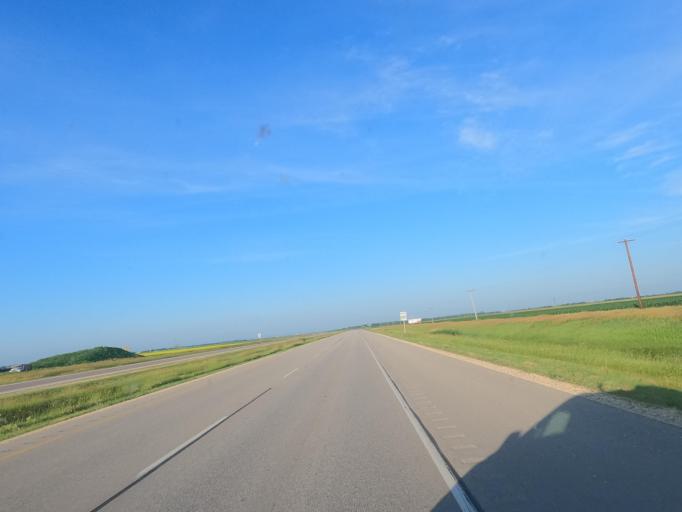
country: CA
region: Manitoba
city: Winnipeg
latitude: 50.0508
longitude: -97.0638
